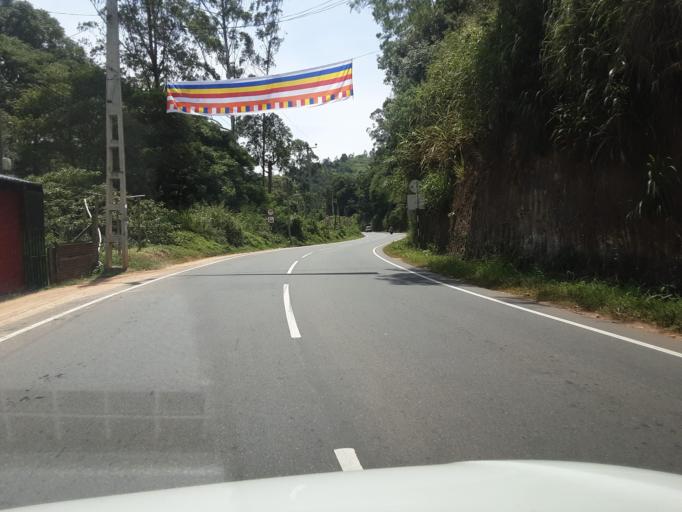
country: LK
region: Central
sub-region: Nuwara Eliya District
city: Nuwara Eliya
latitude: 6.9129
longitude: 80.9070
